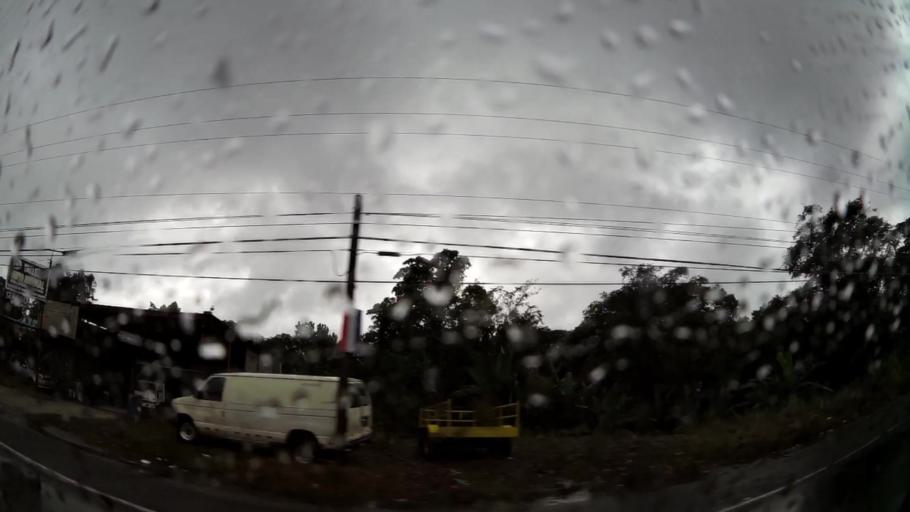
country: PA
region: Colon
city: Buena Vista
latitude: 9.2749
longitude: -79.6976
